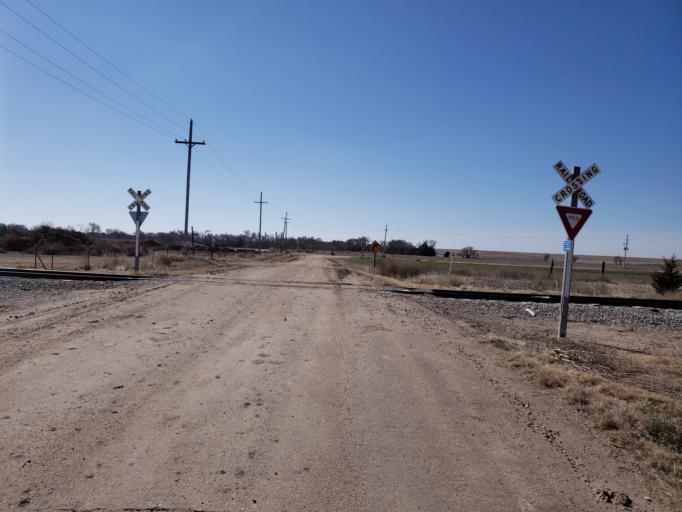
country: US
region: Kansas
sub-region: Ness County
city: Ness City
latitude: 38.4519
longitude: -99.9215
